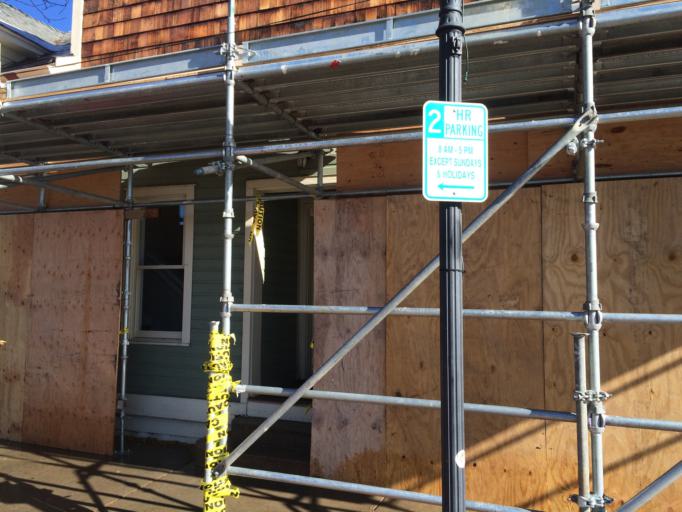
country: US
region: Colorado
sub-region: Boulder County
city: Louisville
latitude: 39.9770
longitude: -105.1308
